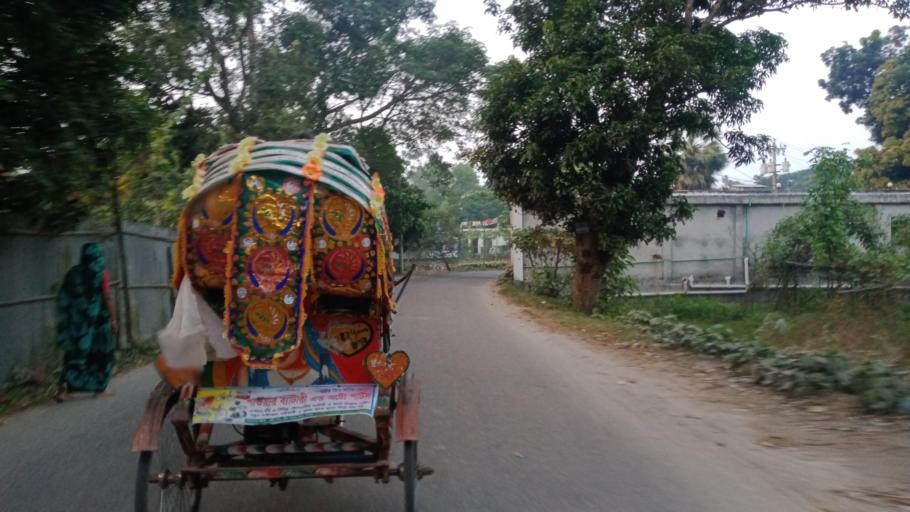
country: BD
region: Chittagong
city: Hajiganj
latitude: 23.3766
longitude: 90.9840
